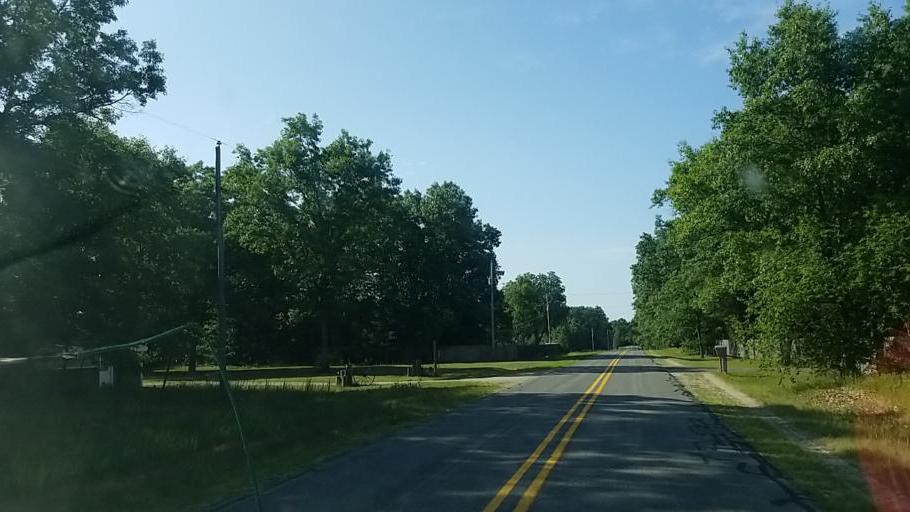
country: US
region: Michigan
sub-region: Muskegon County
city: Twin Lake
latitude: 43.4658
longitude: -86.1933
